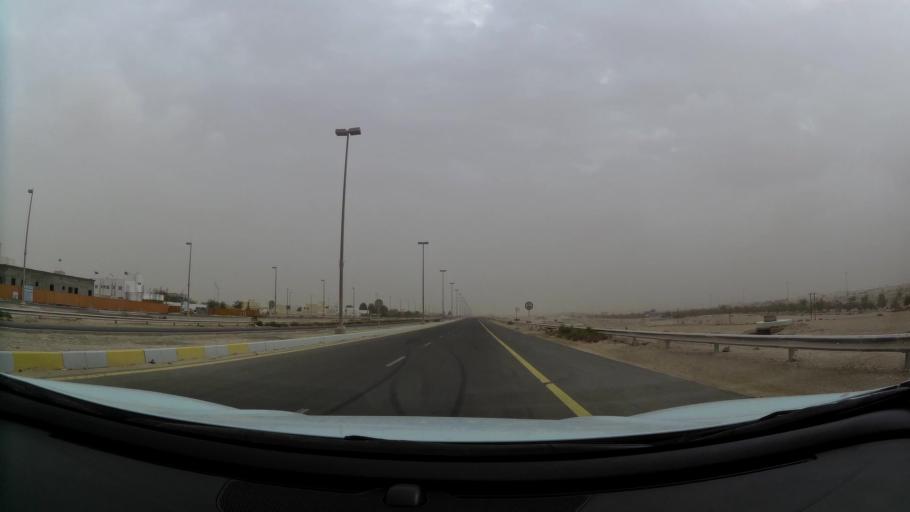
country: AE
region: Abu Dhabi
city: Abu Dhabi
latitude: 24.4205
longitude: 54.7439
